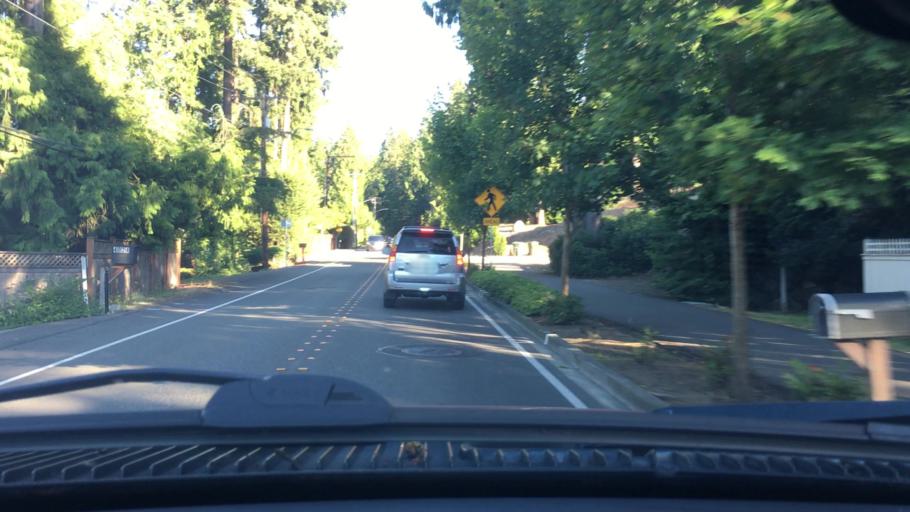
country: US
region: Washington
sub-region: King County
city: West Lake Sammamish
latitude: 47.5736
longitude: -122.1088
